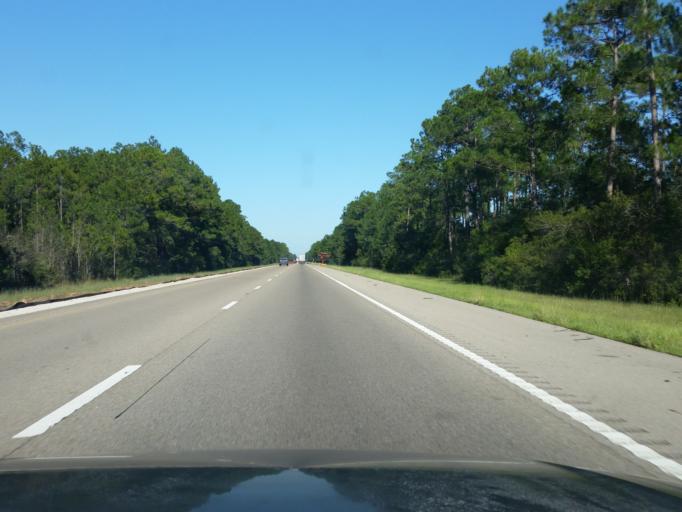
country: US
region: Mississippi
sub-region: Hancock County
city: Kiln
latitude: 30.3326
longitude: -89.5170
